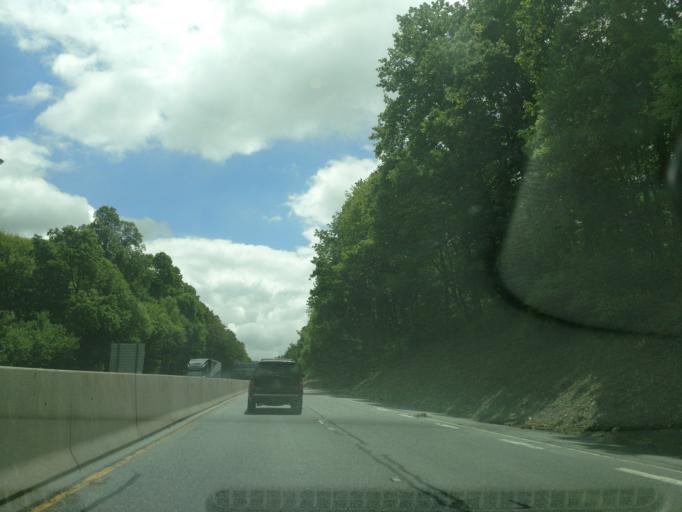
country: US
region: Pennsylvania
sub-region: Lebanon County
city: Cornwall
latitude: 40.2636
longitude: -76.4345
